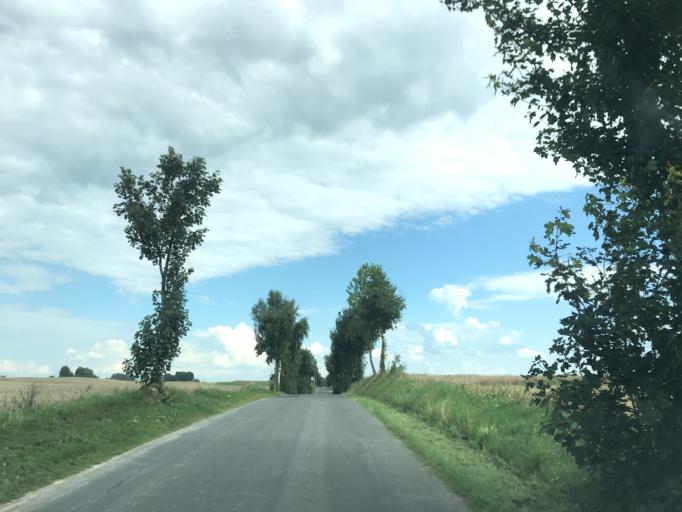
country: PL
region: Kujawsko-Pomorskie
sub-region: Powiat brodnicki
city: Brzozie
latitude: 53.3290
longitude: 19.6732
